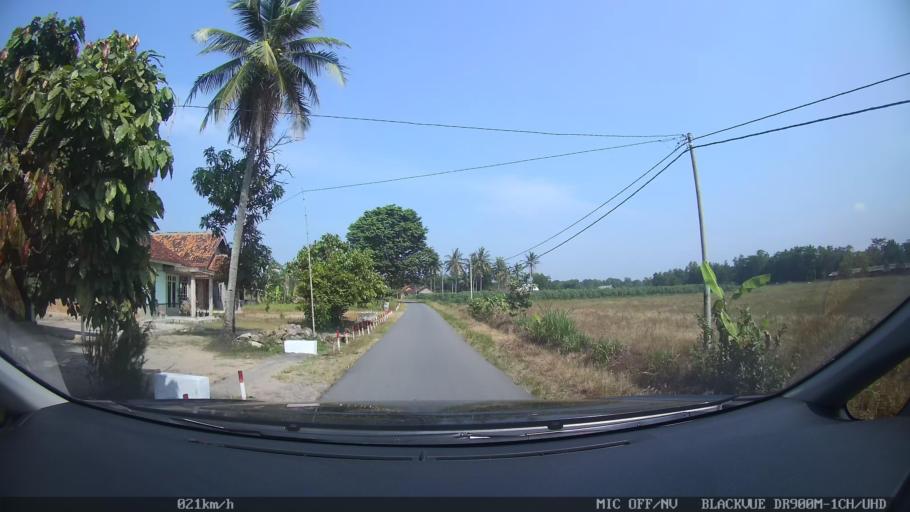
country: ID
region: Lampung
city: Natar
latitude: -5.2552
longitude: 105.2086
